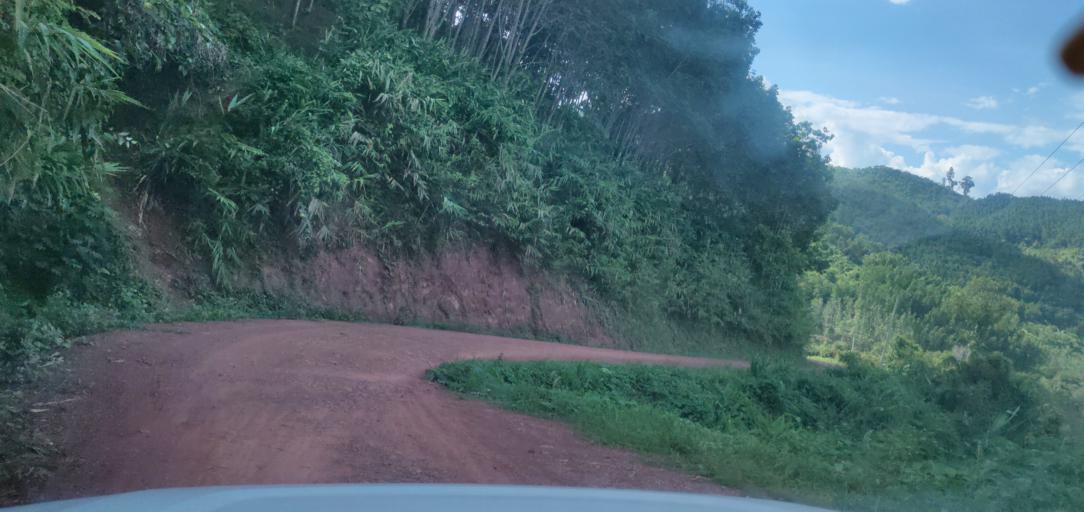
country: LA
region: Phongsali
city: Phongsali
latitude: 21.4362
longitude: 102.0413
